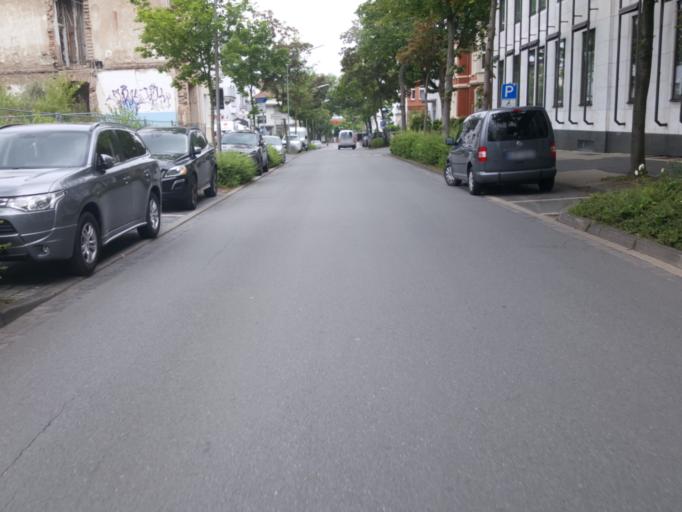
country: DE
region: North Rhine-Westphalia
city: Bad Oeynhausen
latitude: 52.2036
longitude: 8.7991
